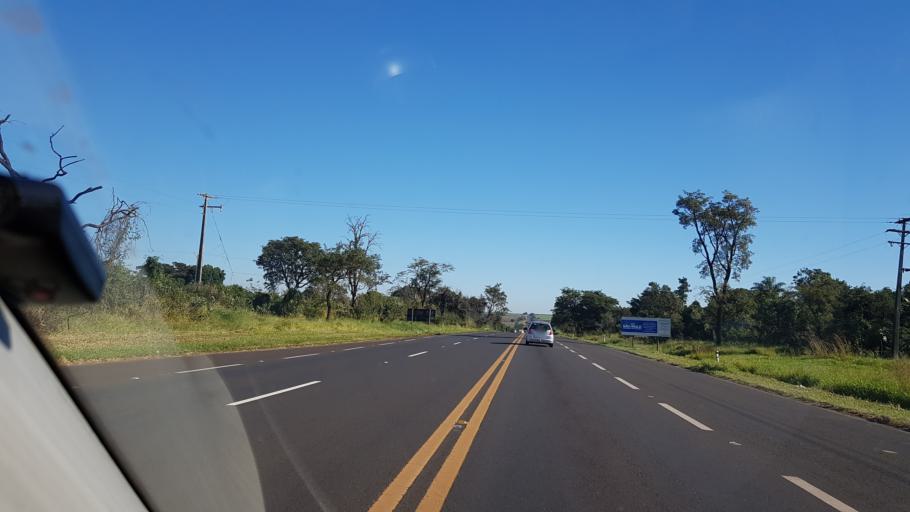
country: BR
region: Sao Paulo
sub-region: Assis
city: Assis
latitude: -22.6182
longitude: -50.4570
